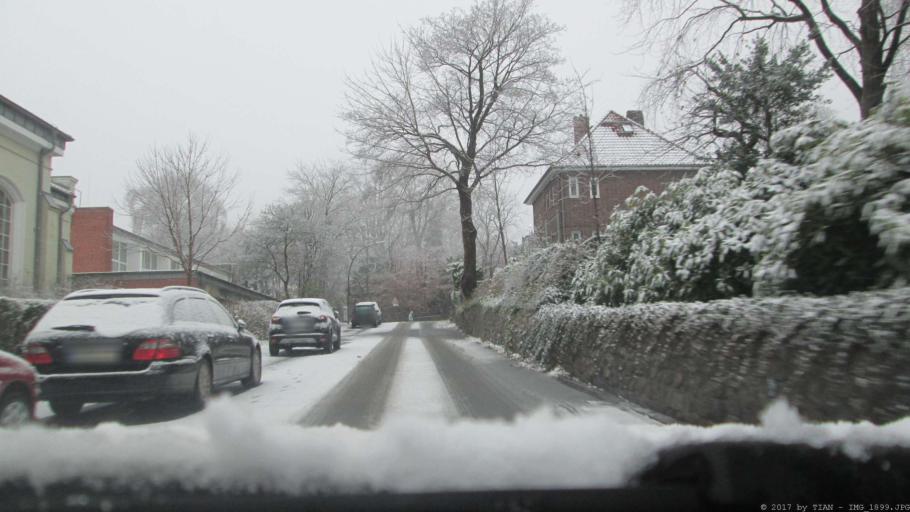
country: DE
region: Schleswig-Holstein
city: Halstenbek
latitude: 53.5634
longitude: 9.8066
